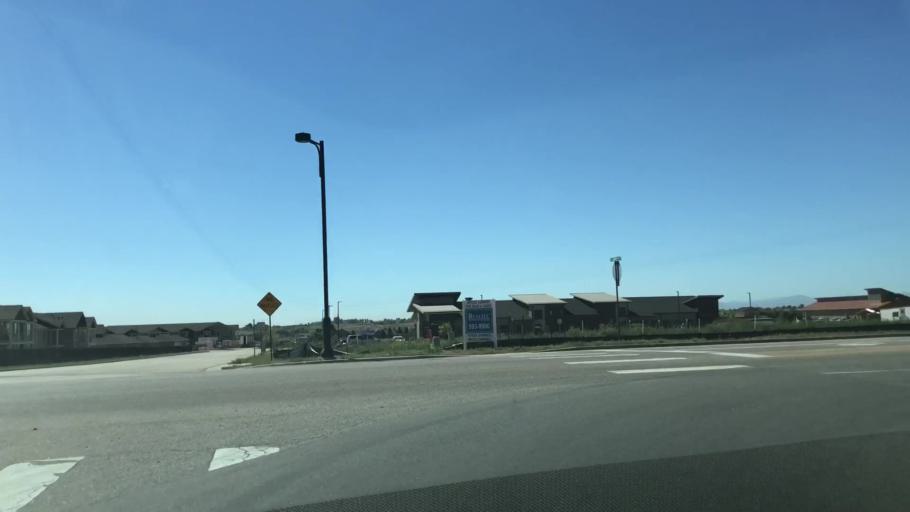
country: US
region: Colorado
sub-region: Weld County
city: Johnstown
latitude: 40.4037
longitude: -104.9741
